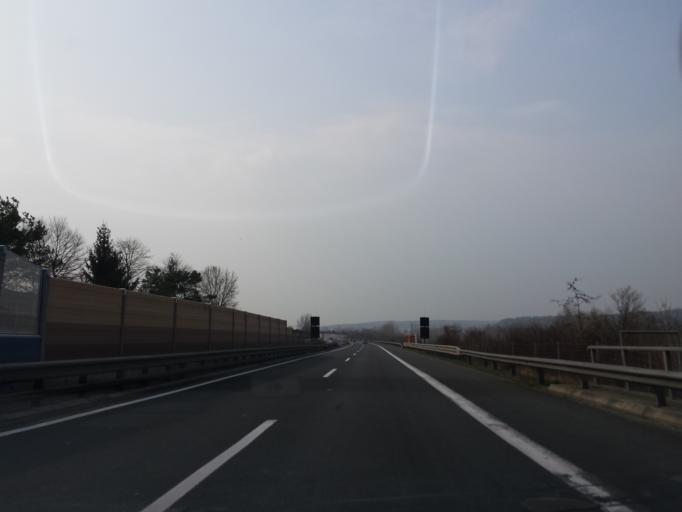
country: AT
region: Styria
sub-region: Politischer Bezirk Hartberg-Fuerstenfeld
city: Nestelbach im Ilztal
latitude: 47.0848
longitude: 15.8762
